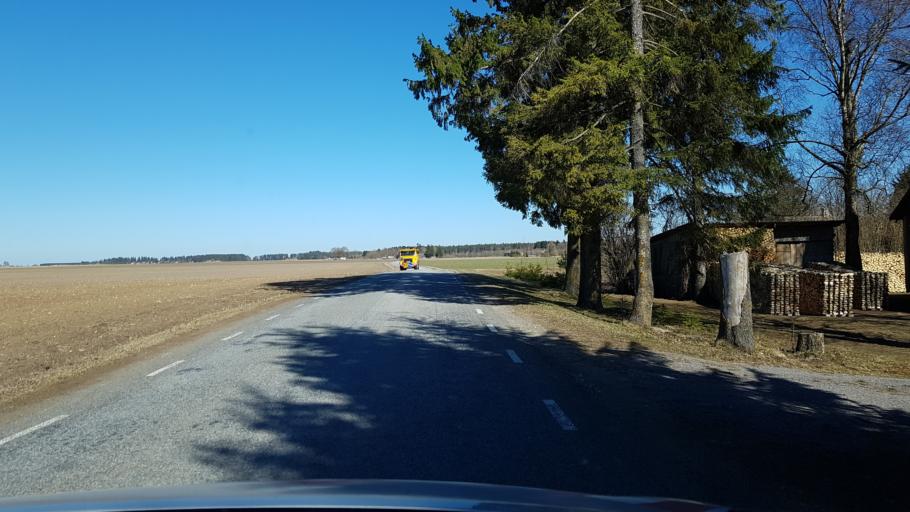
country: EE
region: Laeaene-Virumaa
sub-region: Someru vald
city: Someru
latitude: 59.3922
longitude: 26.4851
